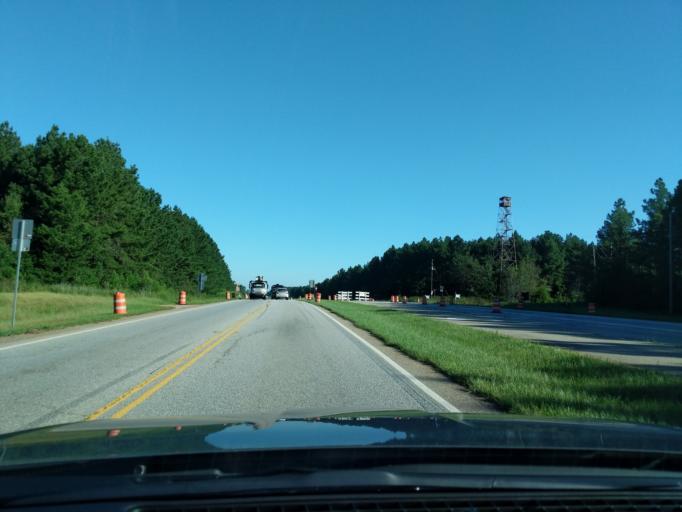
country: US
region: Georgia
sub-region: McDuffie County
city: Thomson
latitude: 33.5482
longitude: -82.5098
